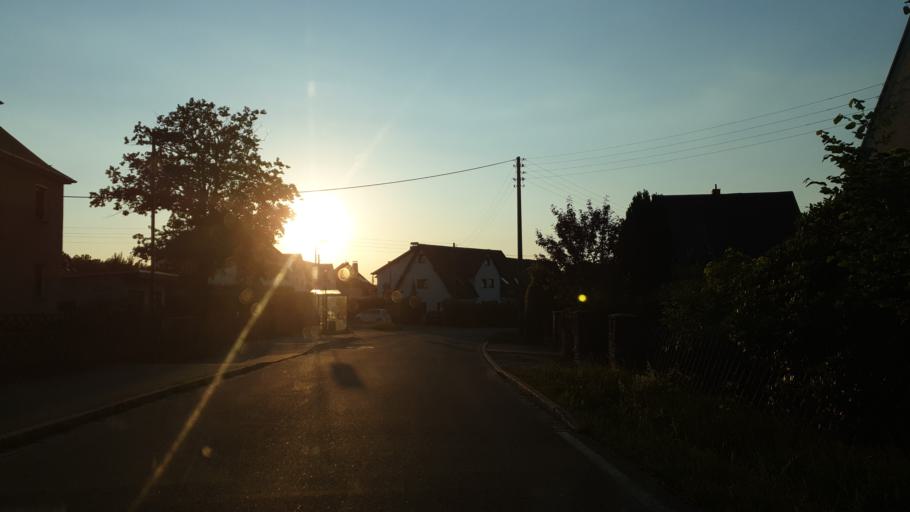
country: DE
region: Saxony
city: Oelsnitz
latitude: 50.7076
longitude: 12.7105
